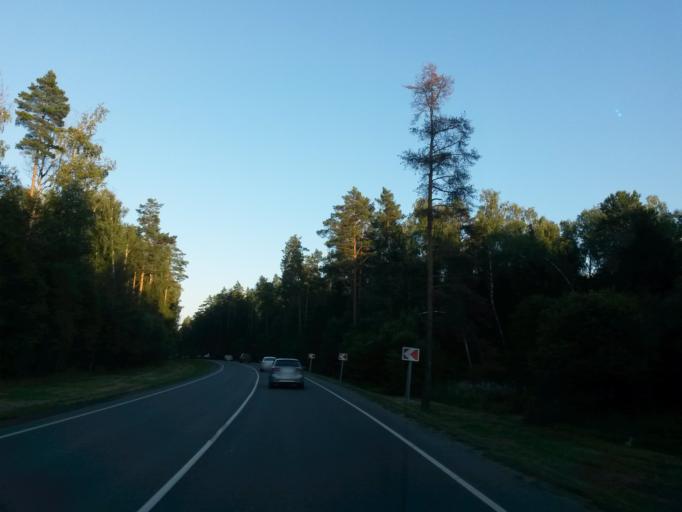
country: RU
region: Moskovskaya
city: Domodedovo
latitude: 55.3690
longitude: 37.6881
